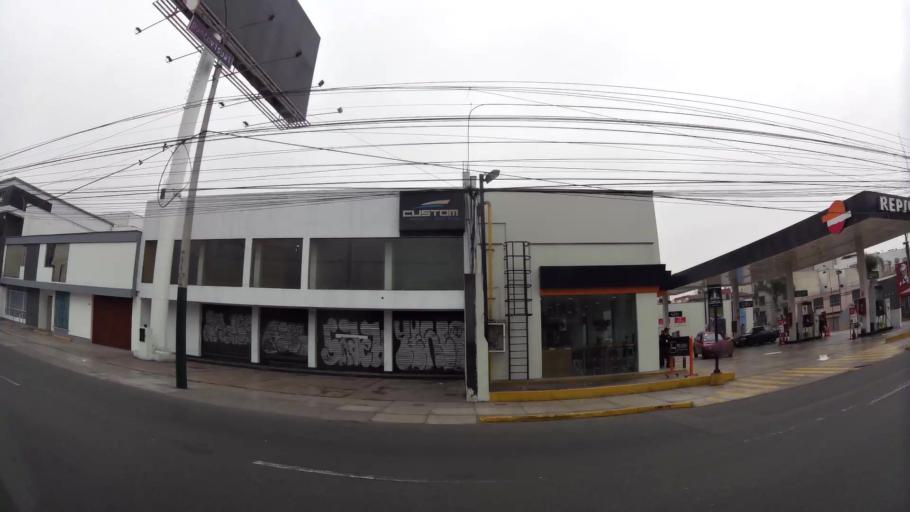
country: PE
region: Lima
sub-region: Lima
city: La Molina
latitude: -12.1104
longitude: -76.9762
